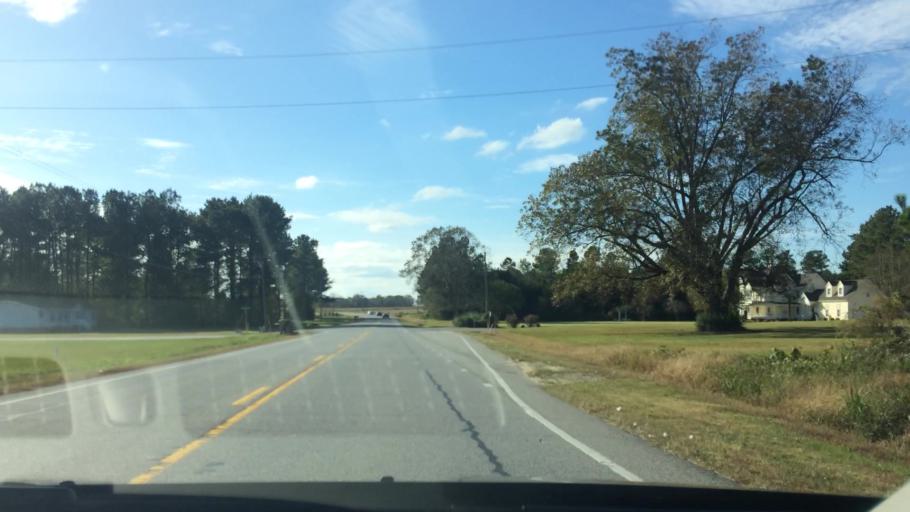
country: US
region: North Carolina
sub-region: Greene County
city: Snow Hill
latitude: 35.4547
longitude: -77.7227
